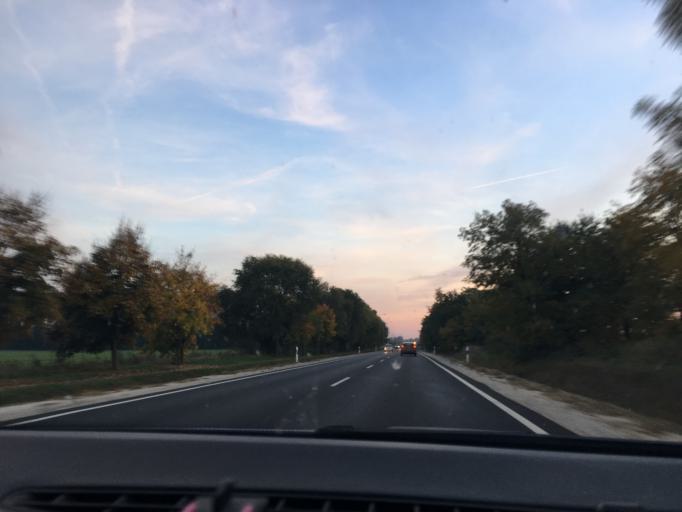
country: HU
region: Hajdu-Bihar
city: Hajduhadhaz
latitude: 47.6529
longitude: 21.6611
